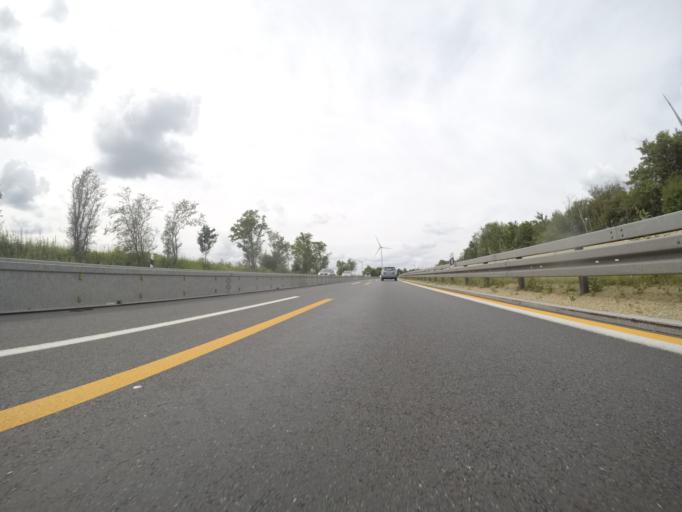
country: DE
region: Bavaria
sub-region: Upper Palatinate
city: Pilsach
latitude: 49.2956
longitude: 11.5545
